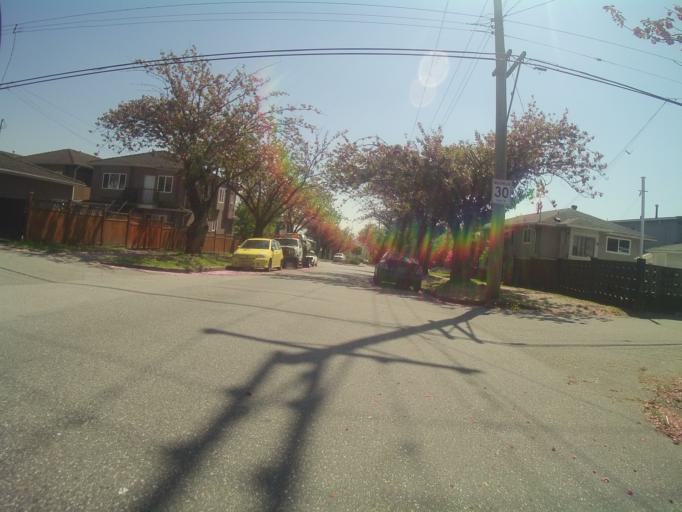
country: CA
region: British Columbia
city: Vancouver
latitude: 49.2159
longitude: -123.0802
